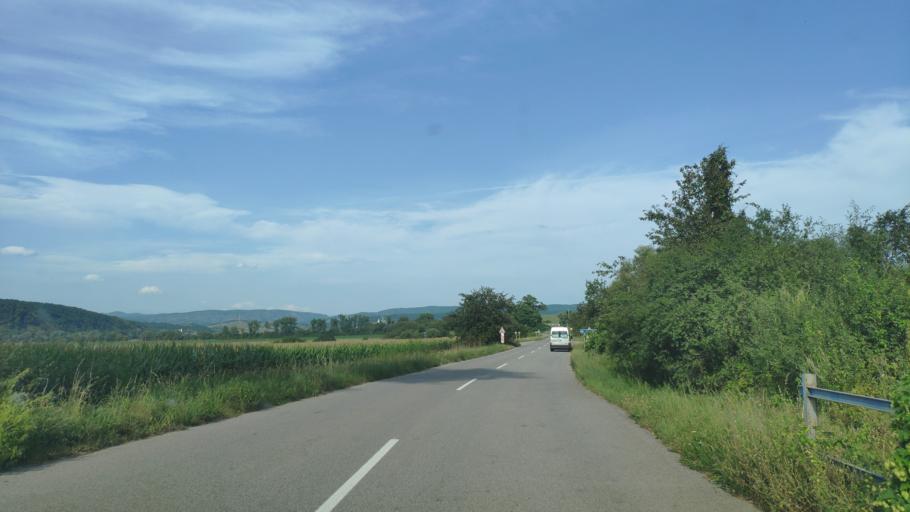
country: HU
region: Borsod-Abauj-Zemplen
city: Putnok
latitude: 48.4792
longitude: 20.3567
